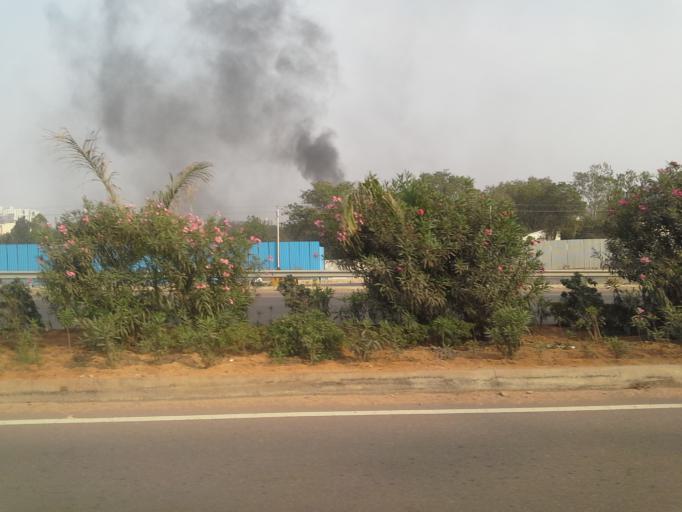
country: IN
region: Telangana
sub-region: Rangareddi
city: Kukatpalli
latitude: 17.4170
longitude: 78.3558
